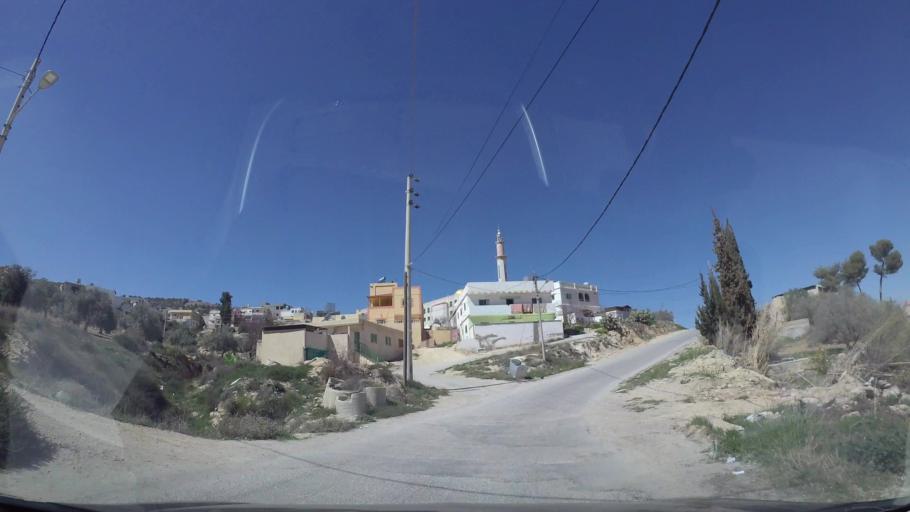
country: JO
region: Tafielah
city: At Tafilah
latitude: 30.8194
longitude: 35.5842
